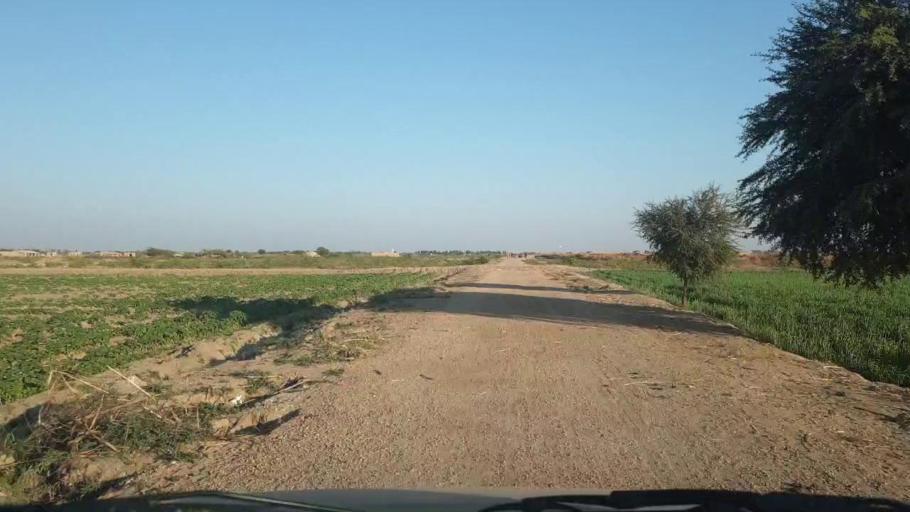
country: PK
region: Sindh
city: Samaro
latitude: 25.3225
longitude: 69.2900
